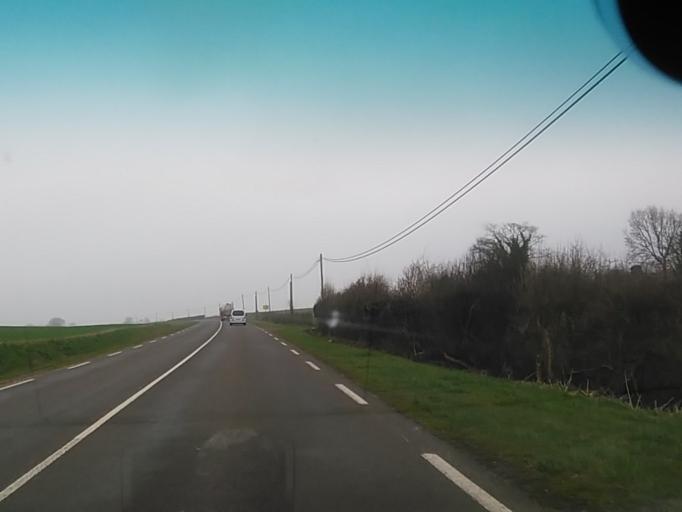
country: FR
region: Lower Normandy
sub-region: Departement de l'Orne
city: Magny-le-Desert
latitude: 48.6287
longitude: -0.2488
